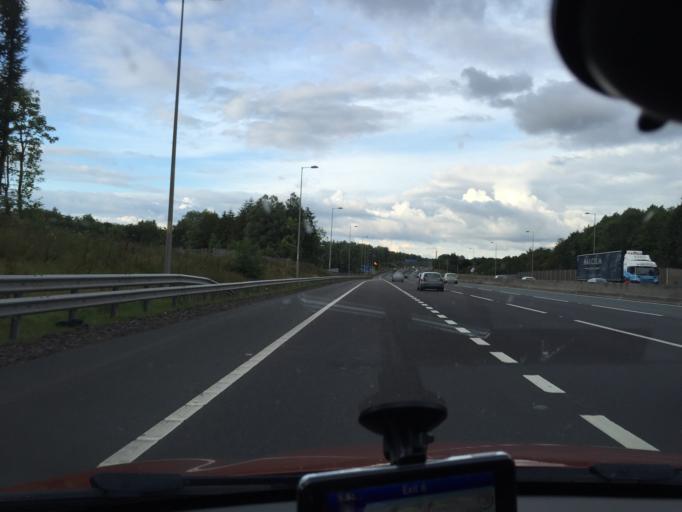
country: GB
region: Scotland
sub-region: North Lanarkshire
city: Glenboig
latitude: 55.9295
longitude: -4.0408
